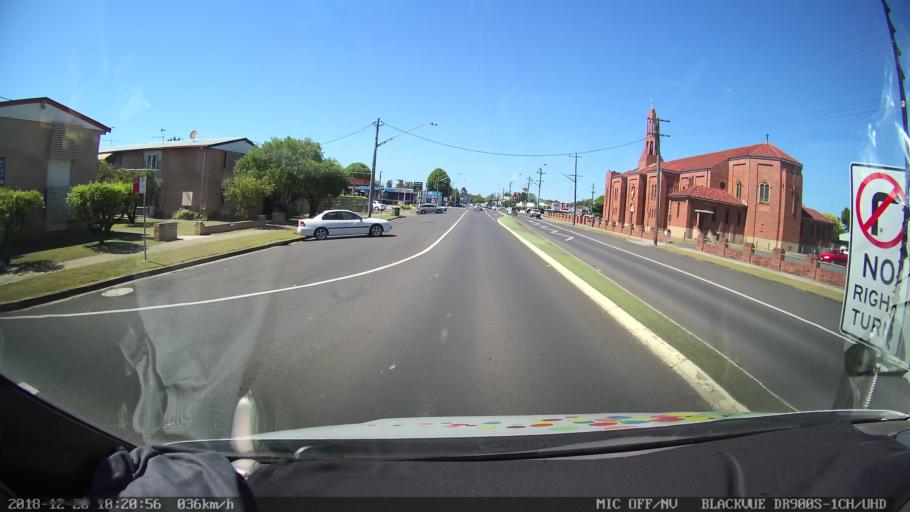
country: AU
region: New South Wales
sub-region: Richmond Valley
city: Casino
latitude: -28.8612
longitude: 153.0464
